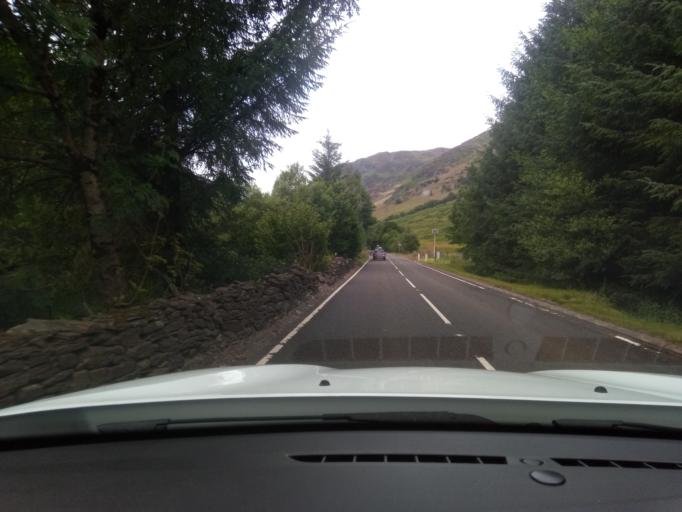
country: GB
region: Scotland
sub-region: Stirling
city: Callander
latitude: 56.3958
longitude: -4.2953
